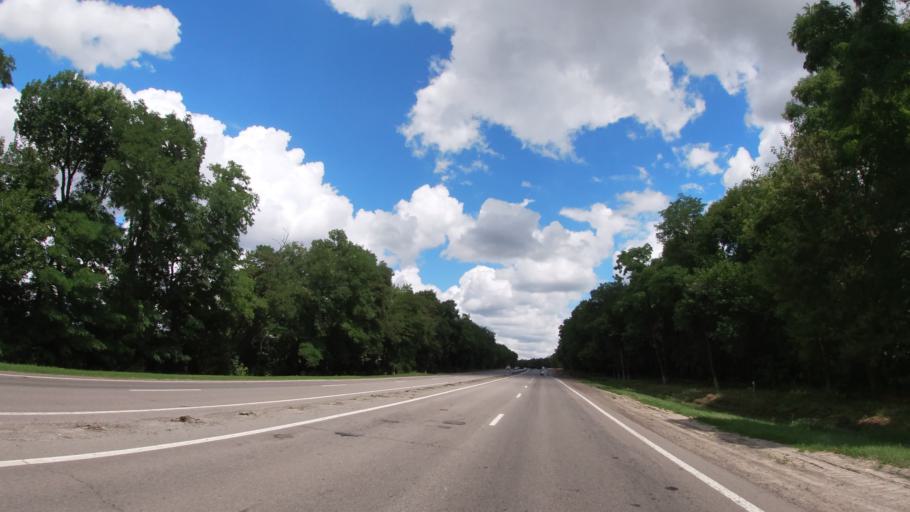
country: RU
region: Belgorod
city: Mayskiy
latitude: 50.4449
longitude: 36.3974
